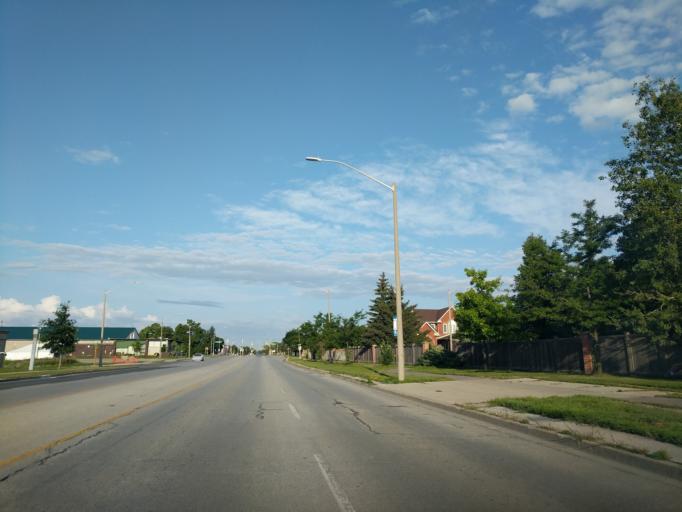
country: CA
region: Ontario
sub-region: York
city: Richmond Hill
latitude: 43.8910
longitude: -79.4357
